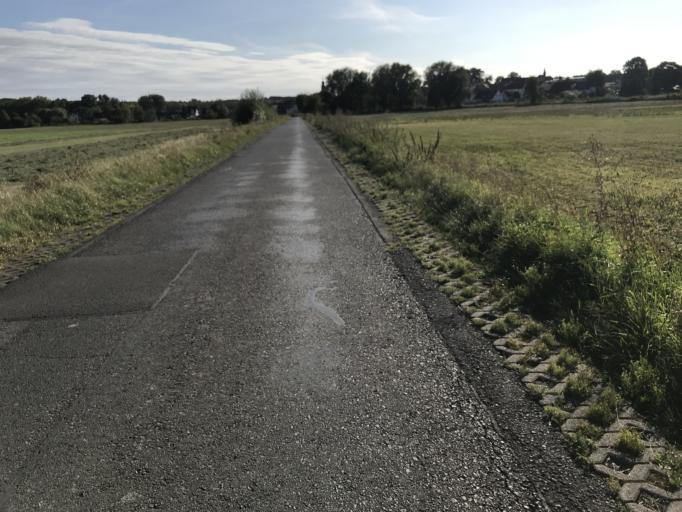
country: DE
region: Hesse
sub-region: Regierungsbezirk Darmstadt
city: Altenstadt
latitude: 50.2724
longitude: 8.9358
